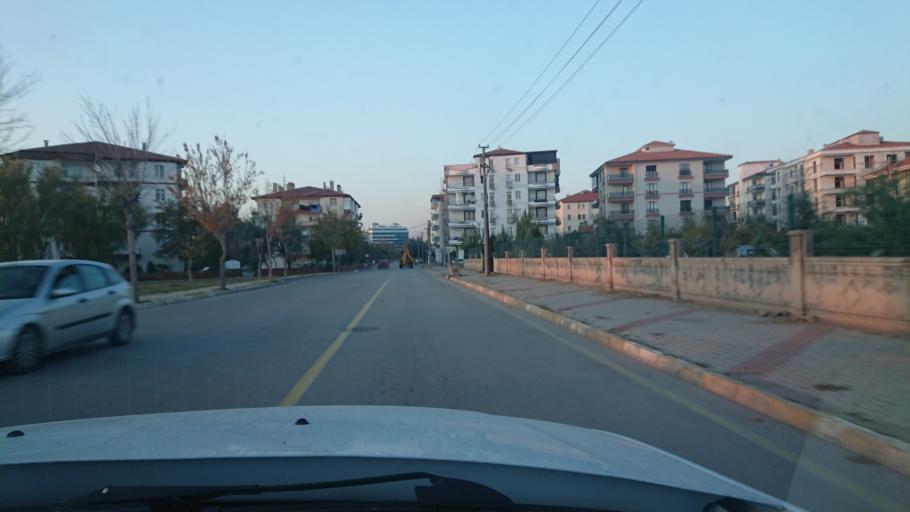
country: TR
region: Aksaray
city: Aksaray
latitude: 38.3531
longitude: 34.0425
